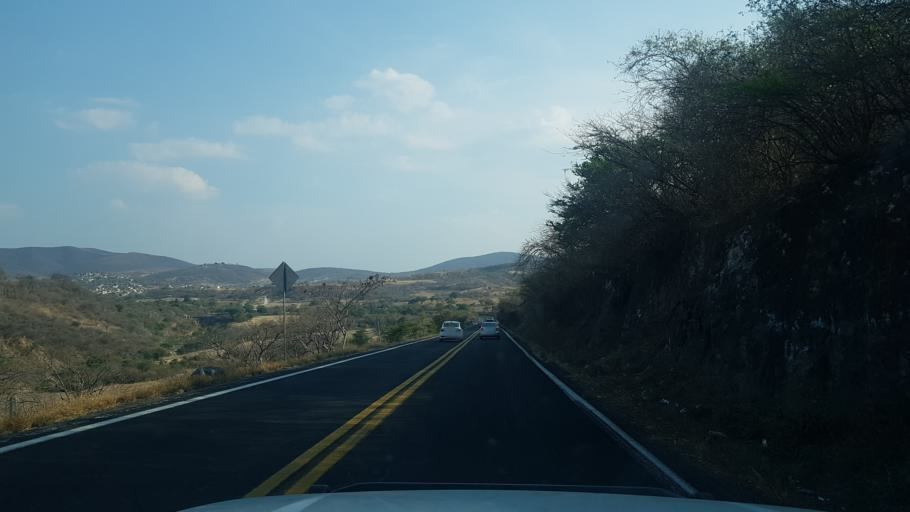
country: MX
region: Puebla
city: Calmeca
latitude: 18.6513
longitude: -98.6445
